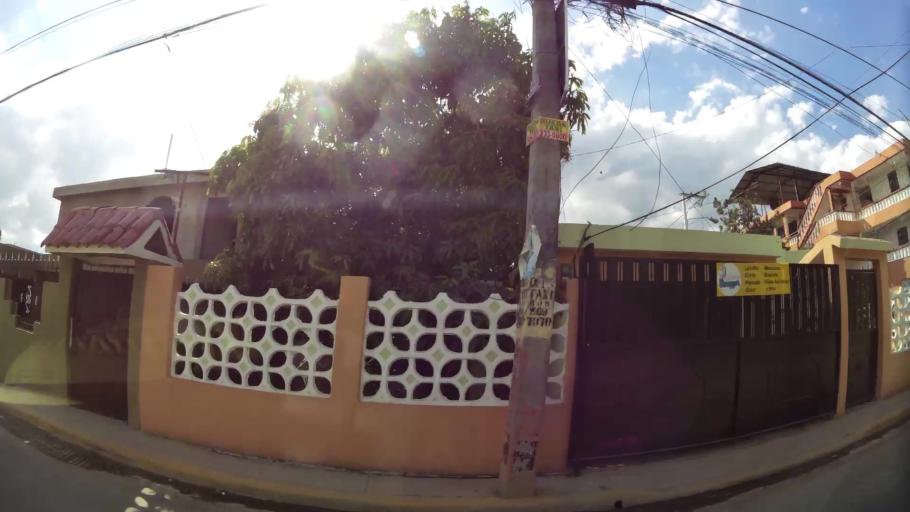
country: DO
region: Nacional
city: Ensanche Luperon
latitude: 18.5399
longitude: -69.8971
